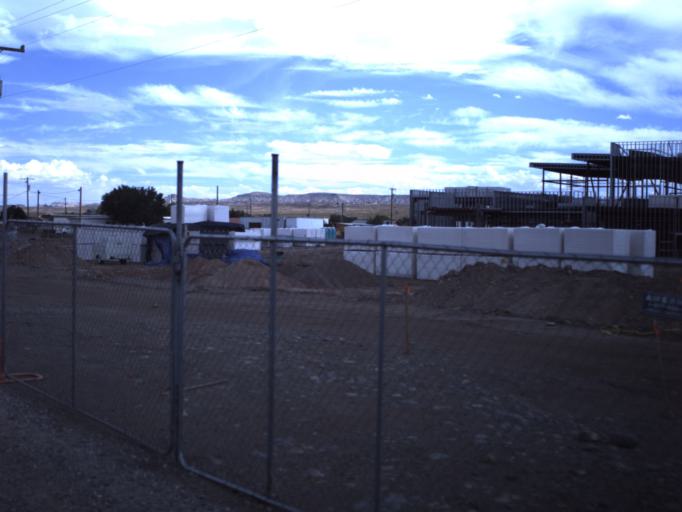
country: US
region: Utah
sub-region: San Juan County
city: Blanding
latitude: 37.2609
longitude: -109.3042
